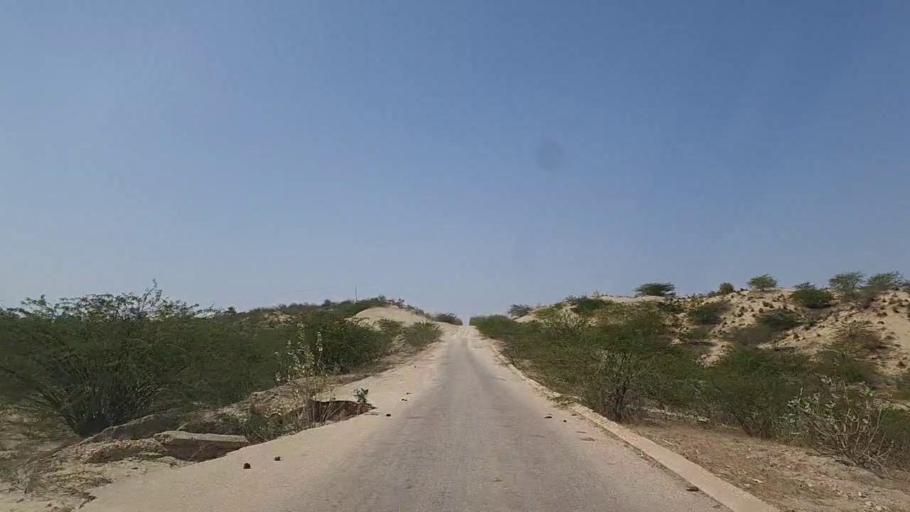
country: PK
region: Sindh
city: Diplo
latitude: 24.5232
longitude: 69.3626
